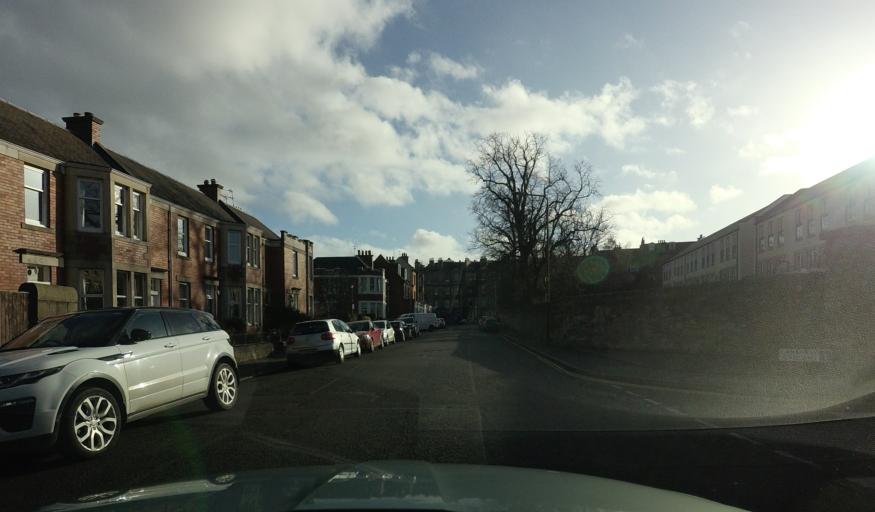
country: GB
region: Scotland
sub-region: Edinburgh
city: Edinburgh
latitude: 55.9722
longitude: -3.2082
